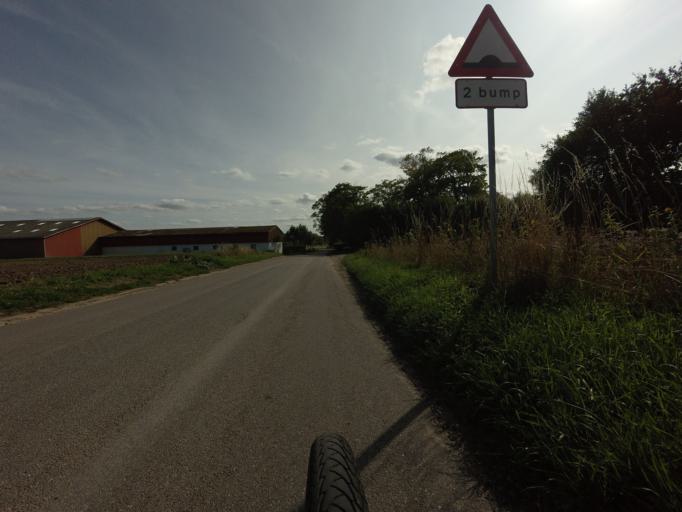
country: DK
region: Zealand
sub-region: Faxe Kommune
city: Fakse
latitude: 55.1876
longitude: 12.1130
